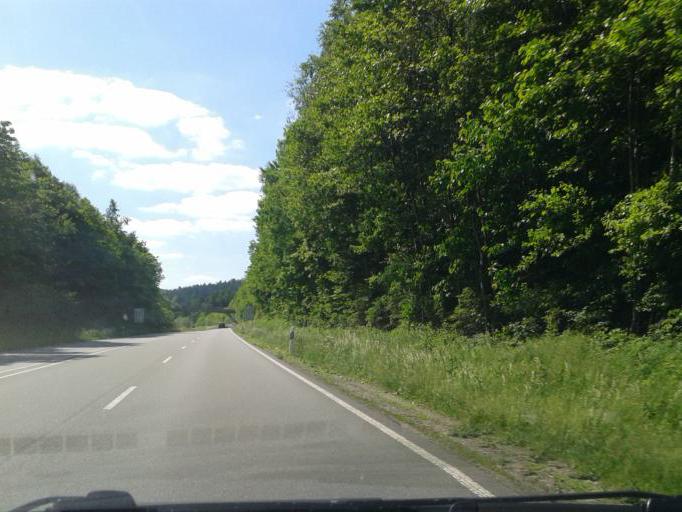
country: DE
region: North Rhine-Westphalia
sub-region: Regierungsbezirk Detmold
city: Horn
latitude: 51.8613
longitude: 8.9447
